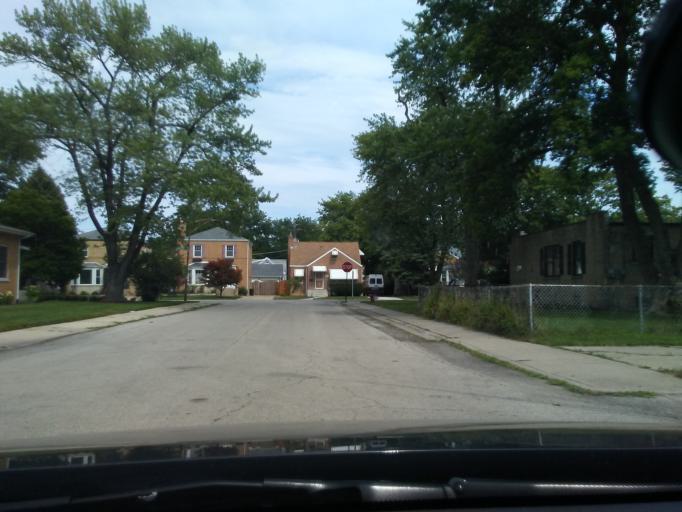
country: US
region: Illinois
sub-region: Cook County
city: Harwood Heights
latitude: 41.9739
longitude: -87.7849
